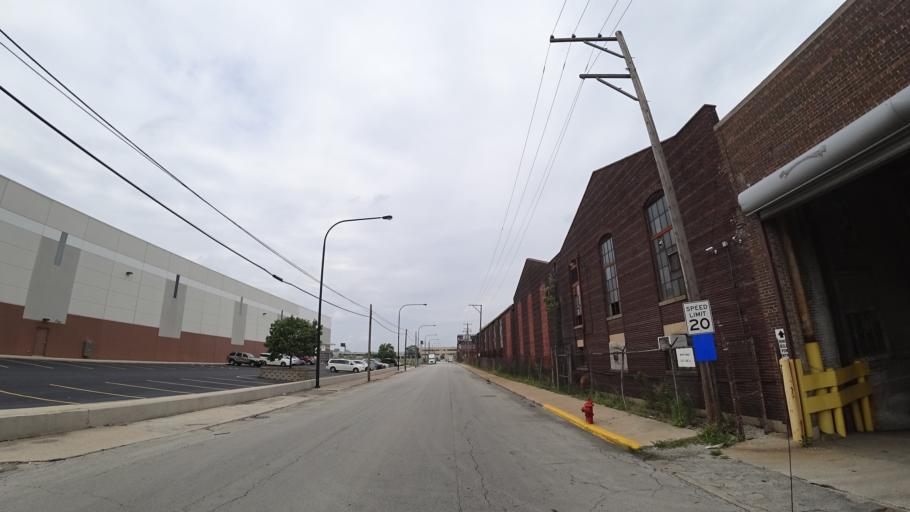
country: US
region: Illinois
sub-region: Cook County
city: Cicero
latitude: 41.8625
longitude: -87.7593
